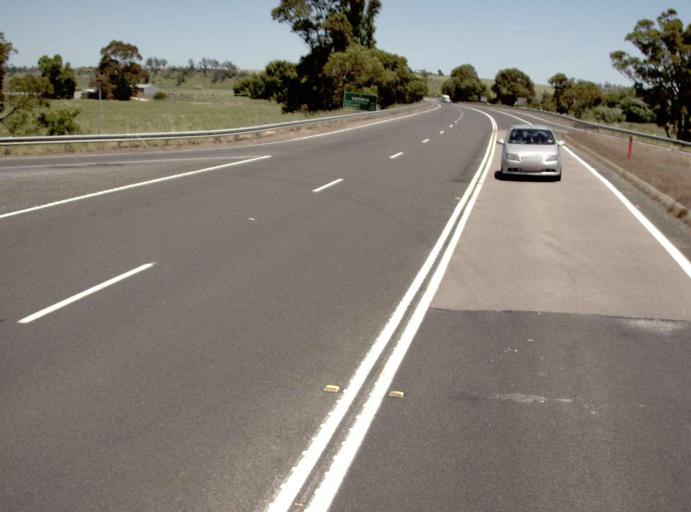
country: AU
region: Victoria
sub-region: East Gippsland
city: Lakes Entrance
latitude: -37.7171
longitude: 148.4530
